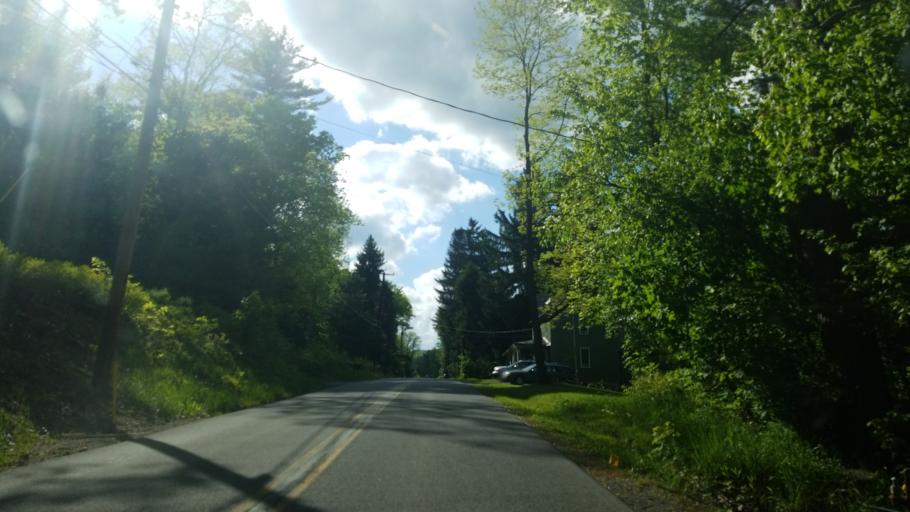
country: US
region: Pennsylvania
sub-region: Clearfield County
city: Troy
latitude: 40.9293
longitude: -78.2925
